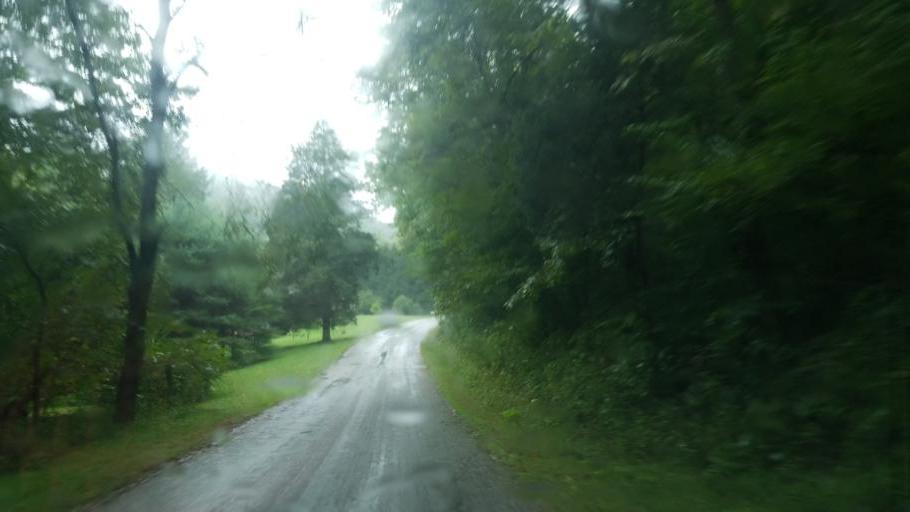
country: US
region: Kentucky
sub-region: Lewis County
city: Vanceburg
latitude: 38.7882
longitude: -83.2570
